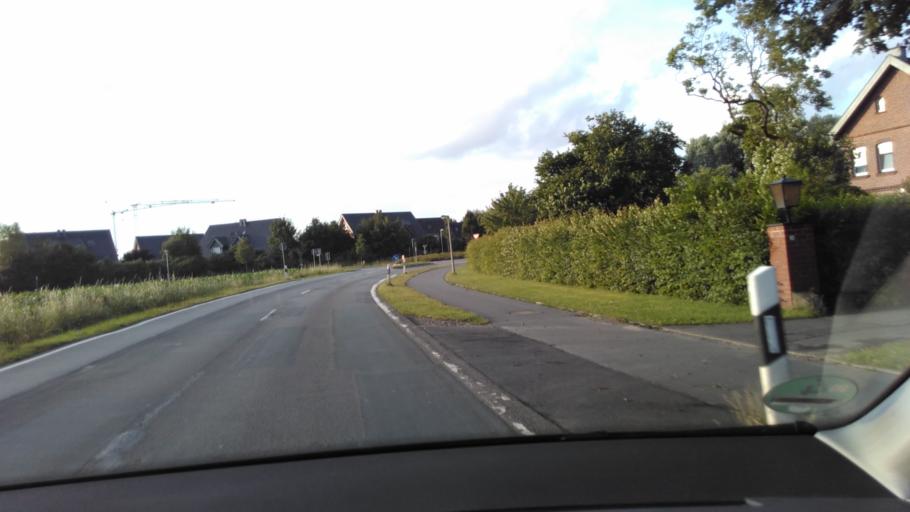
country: DE
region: North Rhine-Westphalia
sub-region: Regierungsbezirk Detmold
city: Verl
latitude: 51.8689
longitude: 8.4991
